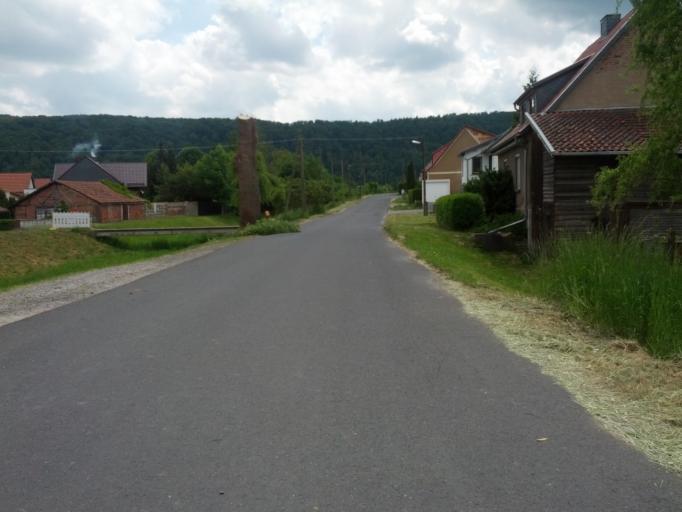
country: DE
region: Thuringia
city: Frankenroda
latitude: 51.1183
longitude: 10.2660
